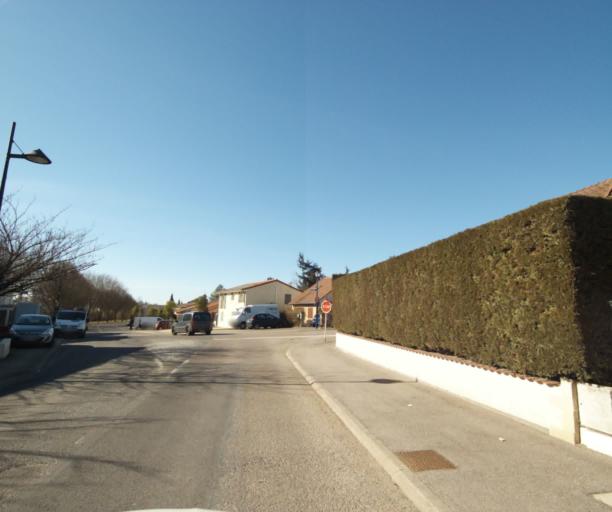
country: FR
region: Lorraine
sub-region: Departement de Meurthe-et-Moselle
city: Ludres
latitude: 48.6239
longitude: 6.1741
